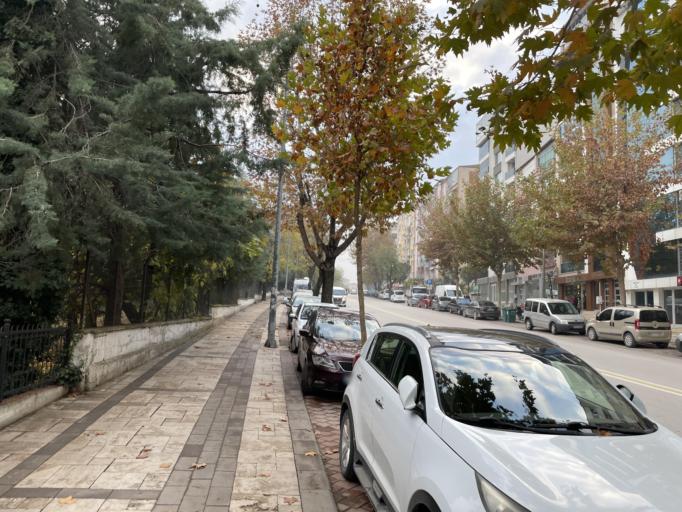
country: TR
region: Denizli
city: Denizli
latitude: 37.7639
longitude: 29.0973
